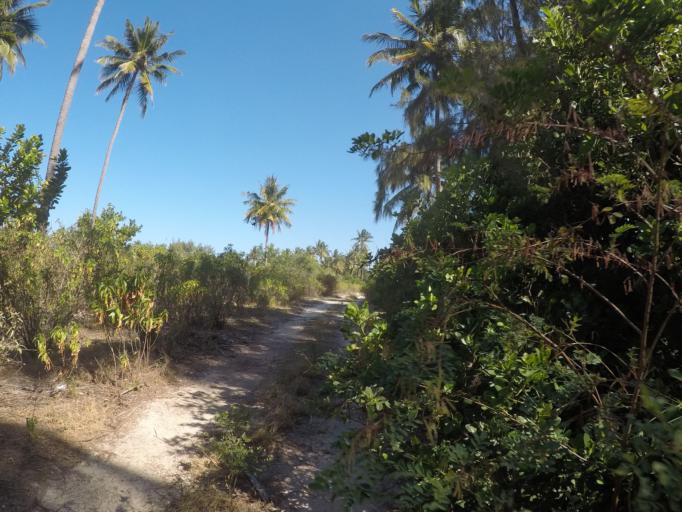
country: TZ
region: Zanzibar Central/South
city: Nganane
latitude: -6.2770
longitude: 39.5351
